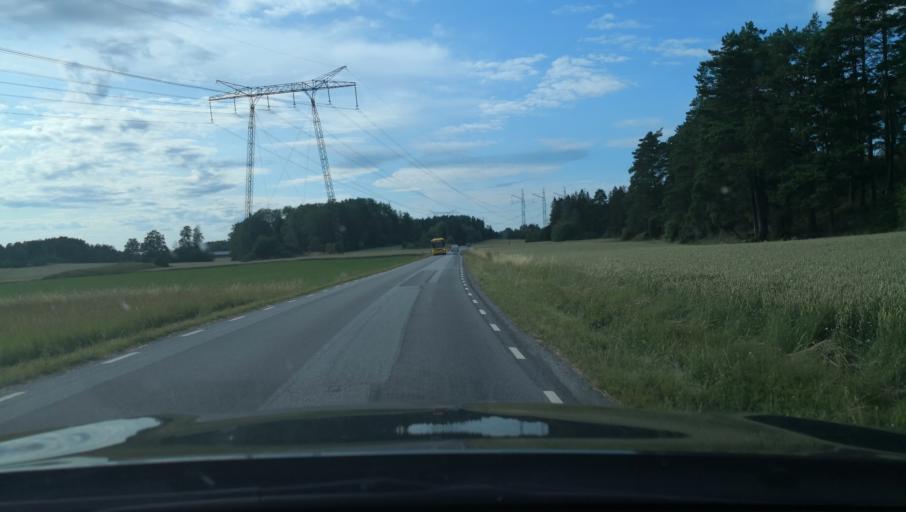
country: SE
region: Uppsala
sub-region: Enkopings Kommun
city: Orsundsbro
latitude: 59.6767
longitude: 17.4165
